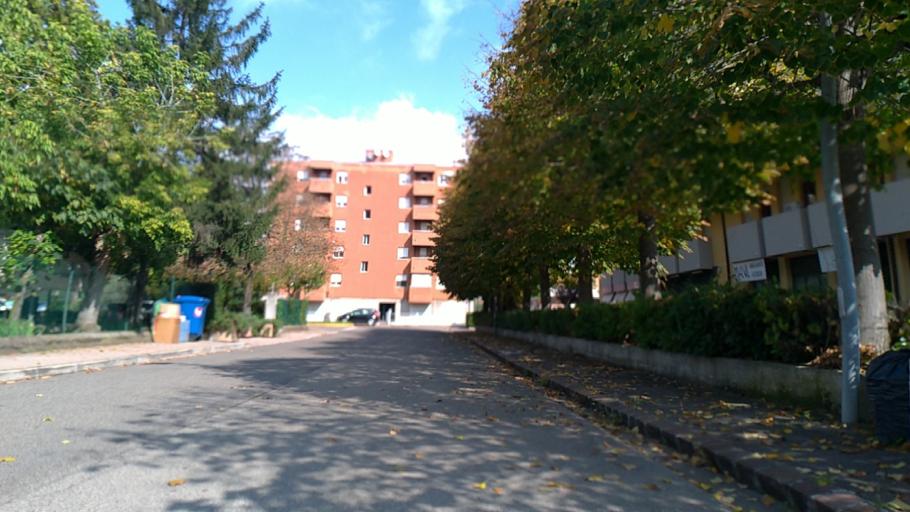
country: IT
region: Emilia-Romagna
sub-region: Provincia di Modena
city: Carpi Centro
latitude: 44.7711
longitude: 10.8729
